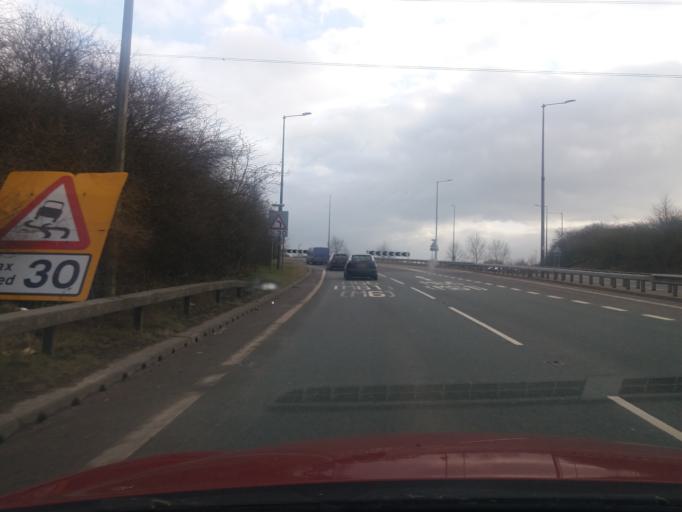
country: GB
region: England
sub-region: Lancashire
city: Clayton-le-Woods
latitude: 53.7194
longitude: -2.6745
